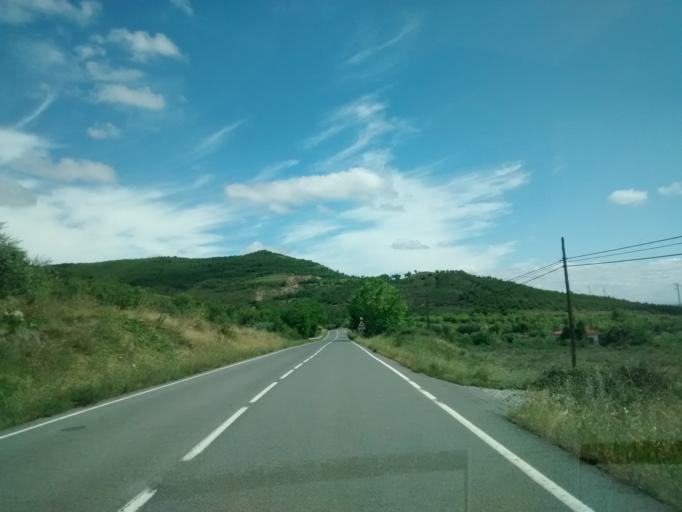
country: ES
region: La Rioja
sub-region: Provincia de La Rioja
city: Leza de Rio Leza
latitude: 42.3413
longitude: -2.4031
